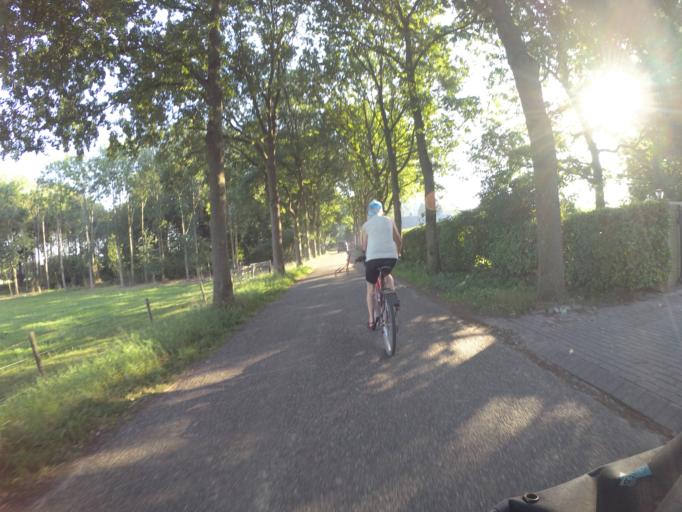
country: NL
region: North Brabant
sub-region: Gemeente Aalburg
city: Aalburg
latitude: 51.7513
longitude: 5.1504
